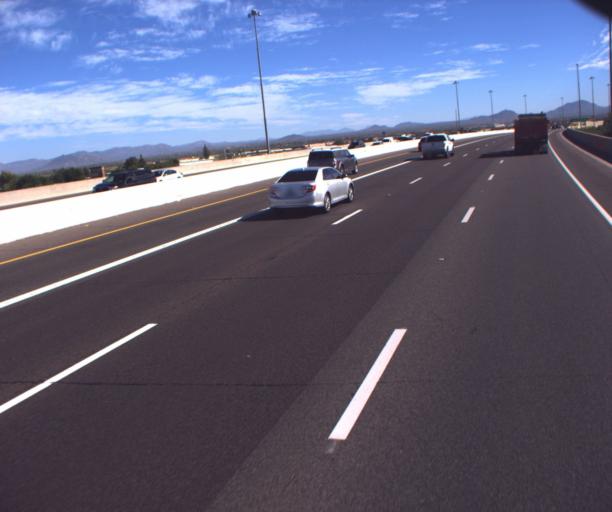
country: US
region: Arizona
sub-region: Maricopa County
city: Paradise Valley
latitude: 33.6714
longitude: -112.0340
